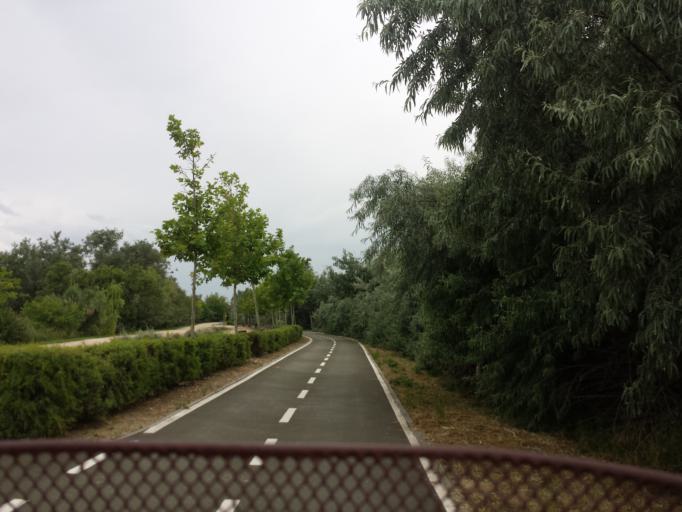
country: ES
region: Aragon
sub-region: Provincia de Zaragoza
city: Almozara
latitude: 41.6772
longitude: -0.9039
